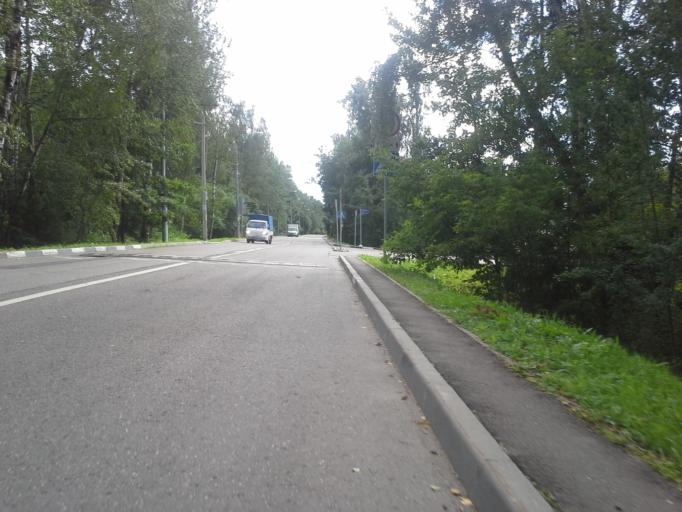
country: RU
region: Moscow
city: Tolstopal'tsevo
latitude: 55.6211
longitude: 37.2156
